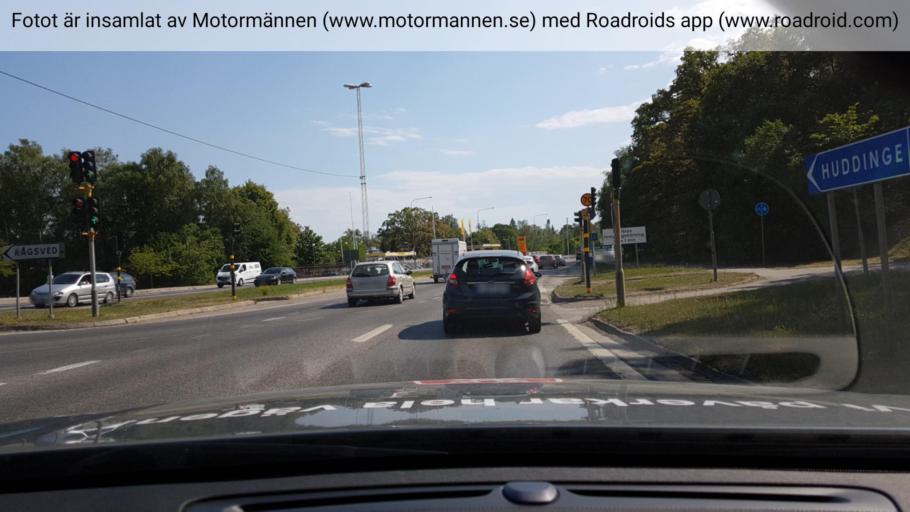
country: SE
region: Stockholm
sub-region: Huddinge Kommun
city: Huddinge
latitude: 59.2570
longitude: 18.0138
